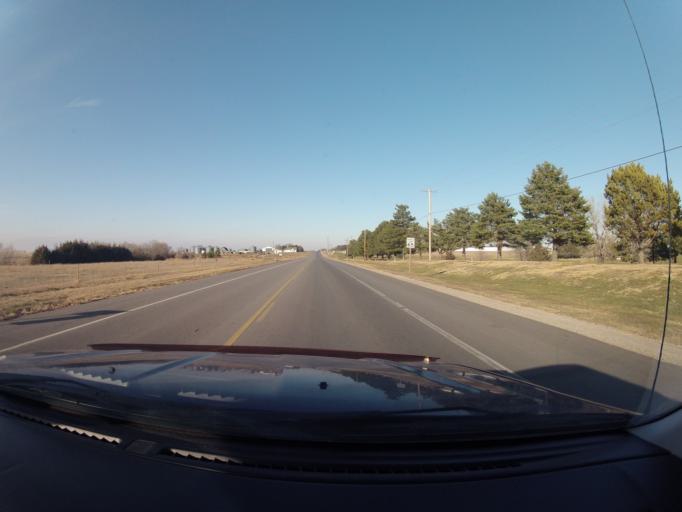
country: US
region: Nebraska
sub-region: Kearney County
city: Minden
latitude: 40.5117
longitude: -98.9519
